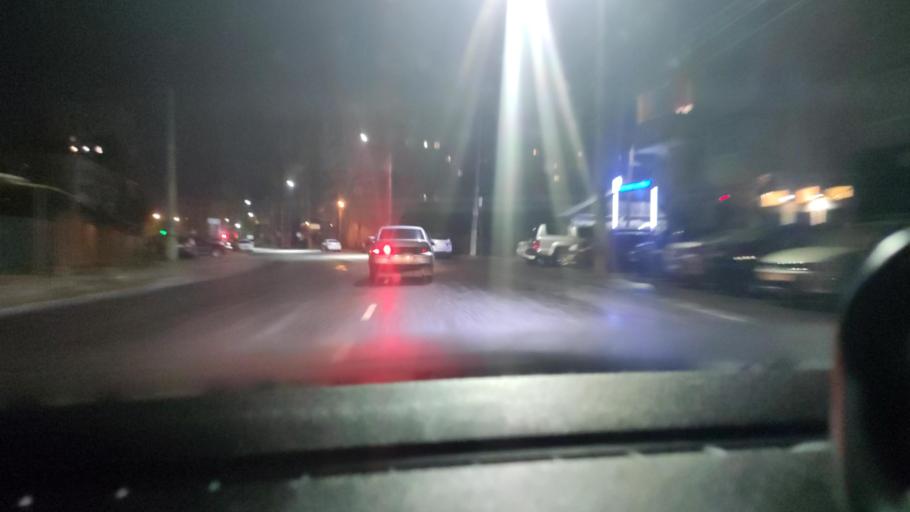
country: RU
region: Voronezj
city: Voronezh
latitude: 51.6509
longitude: 39.1864
